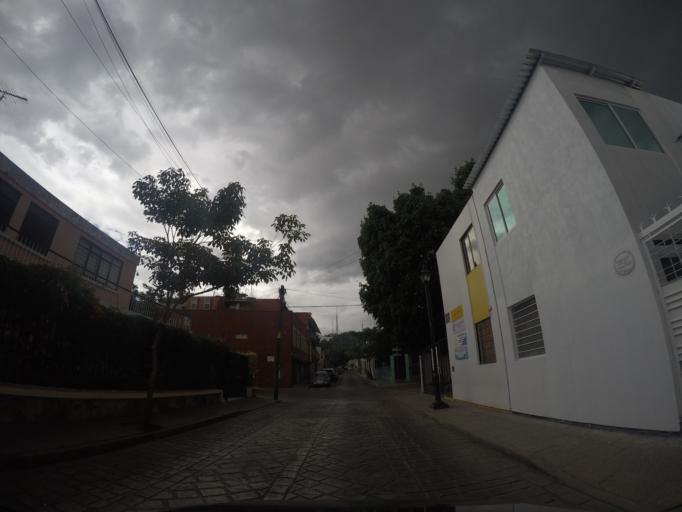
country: MX
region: Oaxaca
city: Oaxaca de Juarez
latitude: 17.0684
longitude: -96.7222
